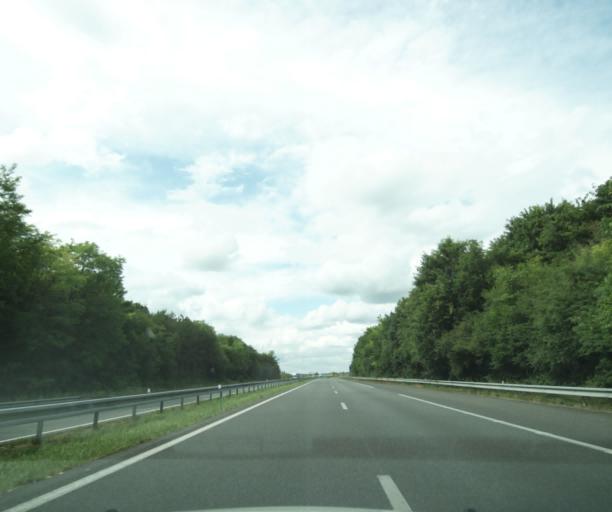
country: FR
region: Centre
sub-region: Departement du Cher
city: Mehun-sur-Yevre
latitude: 47.1454
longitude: 2.1857
